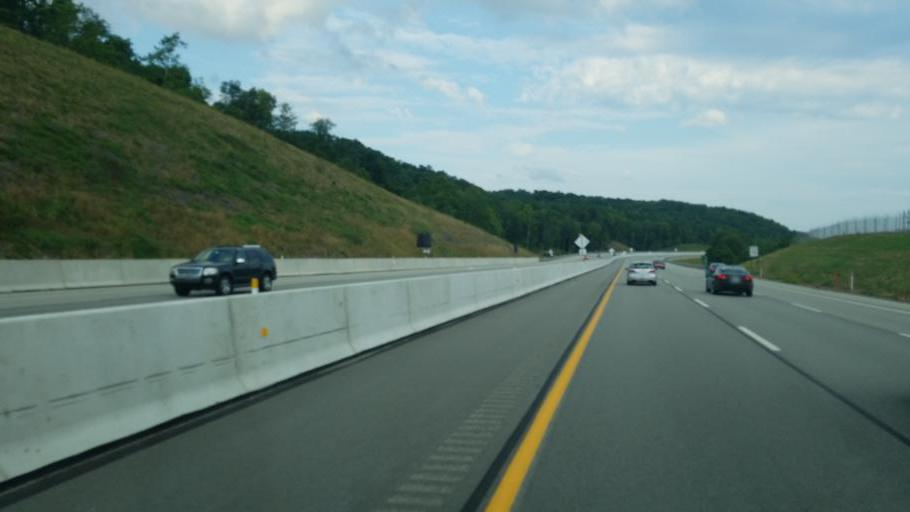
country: US
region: Pennsylvania
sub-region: Allegheny County
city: Russellton
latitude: 40.5728
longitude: -79.8619
